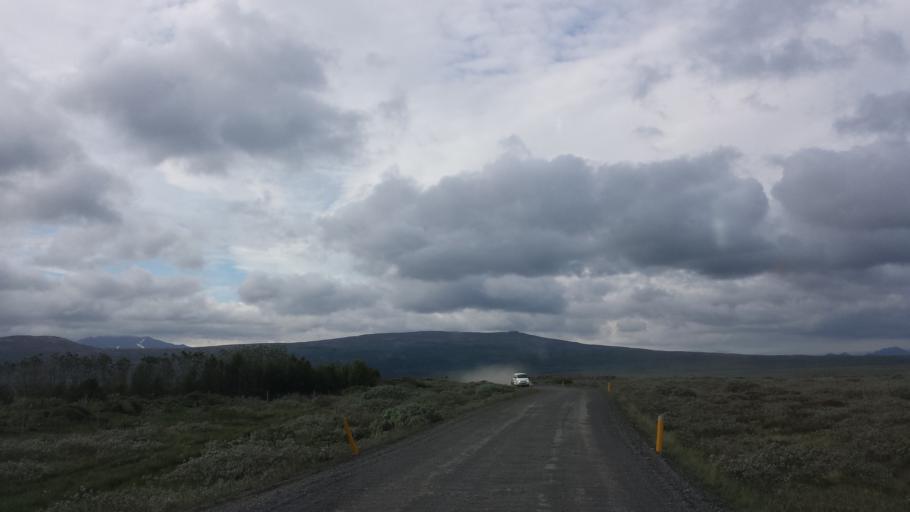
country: IS
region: South
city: Selfoss
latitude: 64.2937
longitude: -20.2364
